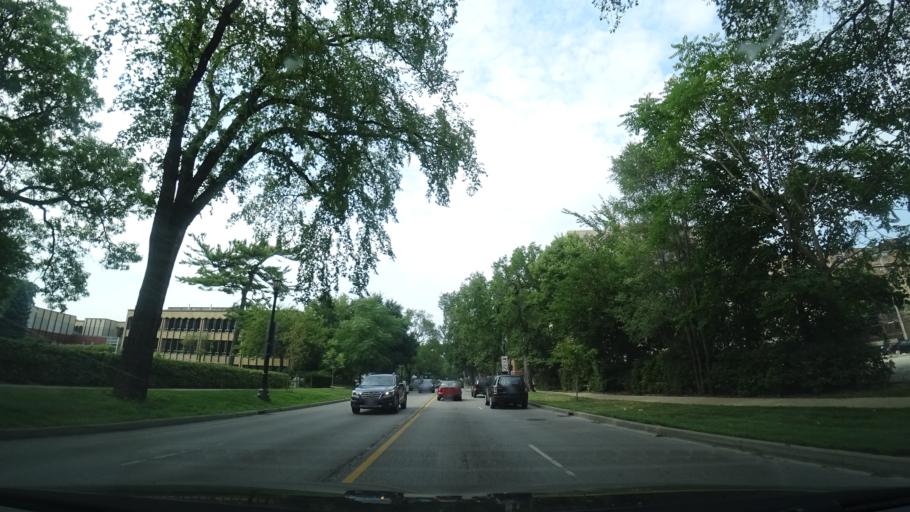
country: US
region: Illinois
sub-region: Cook County
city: Evanston
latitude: 42.0457
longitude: -87.6886
